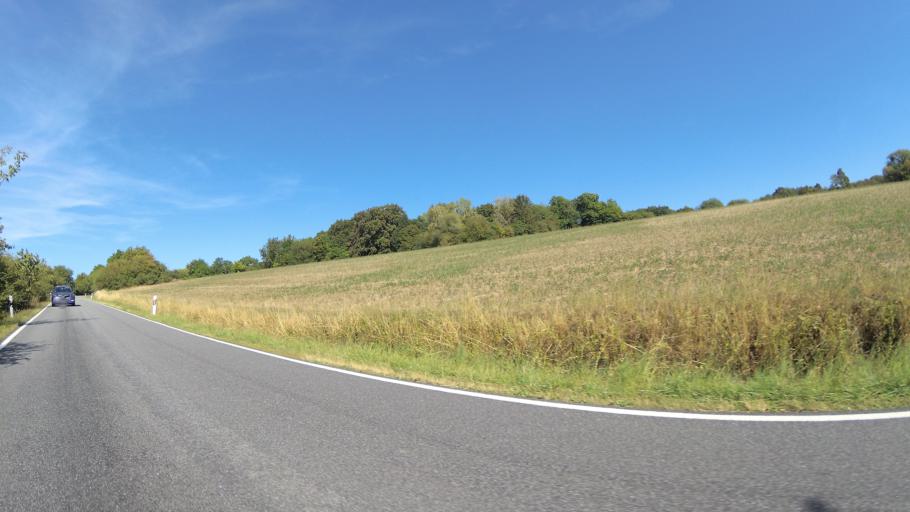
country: DE
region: Saarland
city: Gersheim
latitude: 49.1579
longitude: 7.2507
